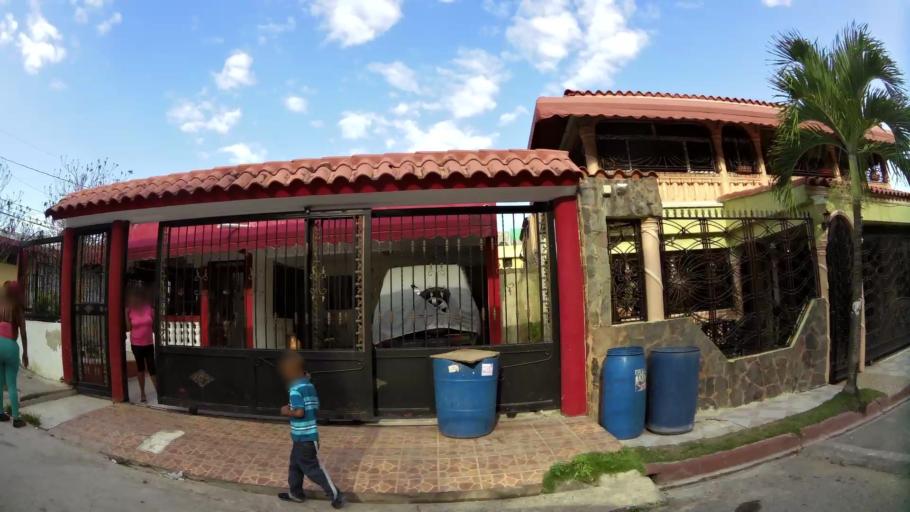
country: DO
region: Nacional
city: Ensanche Luperon
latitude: 18.5547
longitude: -69.8961
